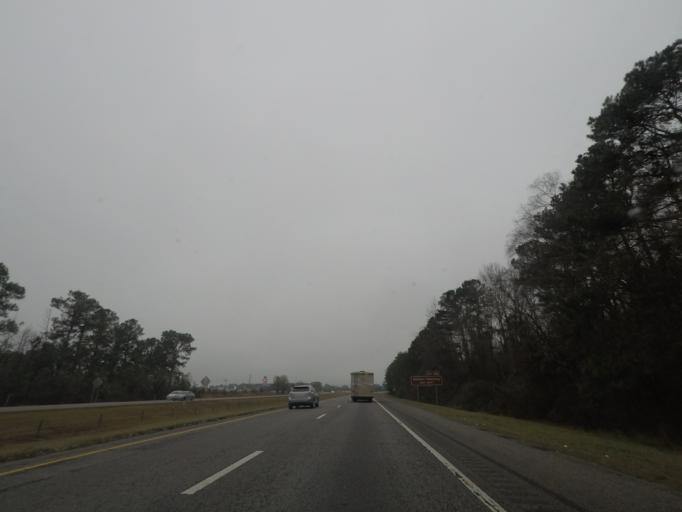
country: US
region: South Carolina
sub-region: Clarendon County
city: Manning
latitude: 33.7102
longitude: -80.2394
